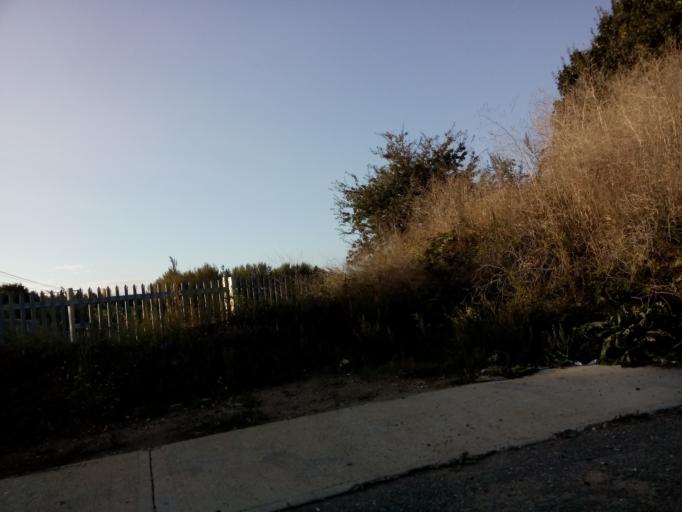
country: GB
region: England
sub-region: Suffolk
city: Bramford
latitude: 52.0679
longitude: 1.1126
